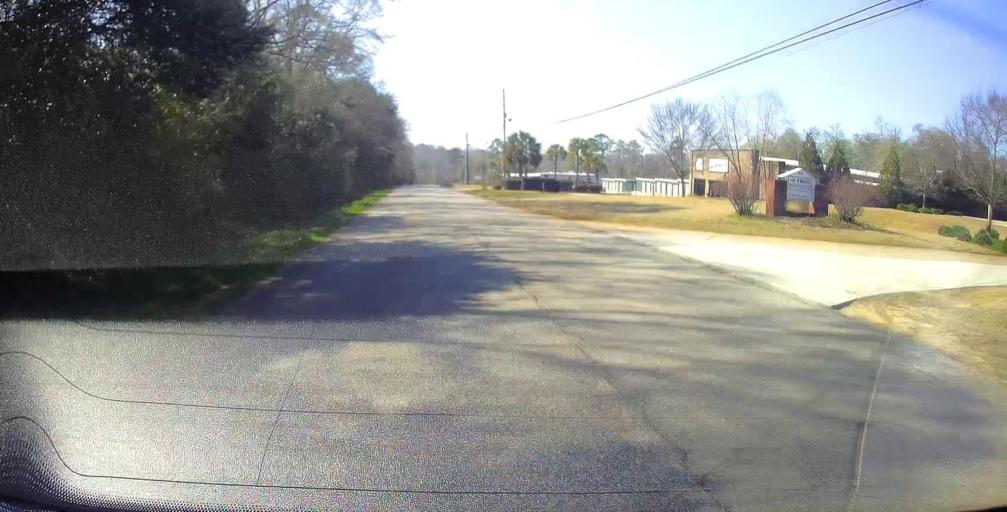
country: US
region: Georgia
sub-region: Houston County
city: Perry
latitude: 32.4659
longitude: -83.7563
